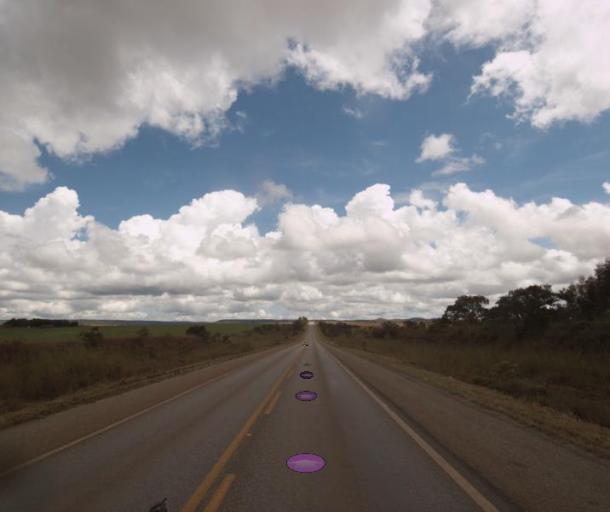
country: BR
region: Goias
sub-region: Pirenopolis
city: Pirenopolis
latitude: -15.7504
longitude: -48.6726
